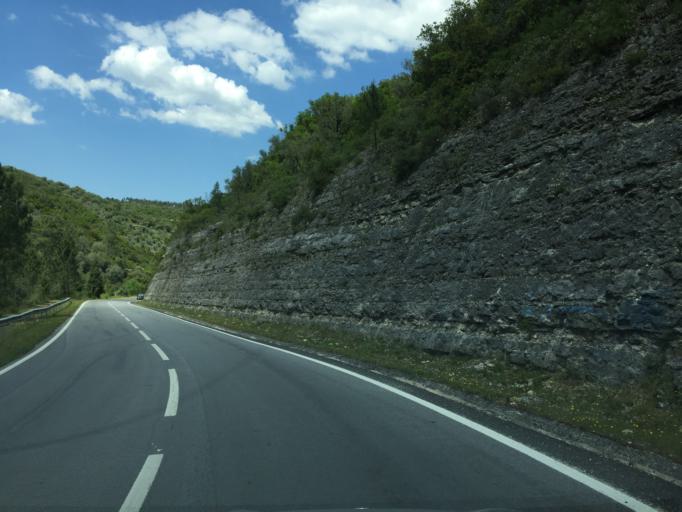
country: PT
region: Santarem
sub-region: Ourem
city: Fatima
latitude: 39.6318
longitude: -8.6514
